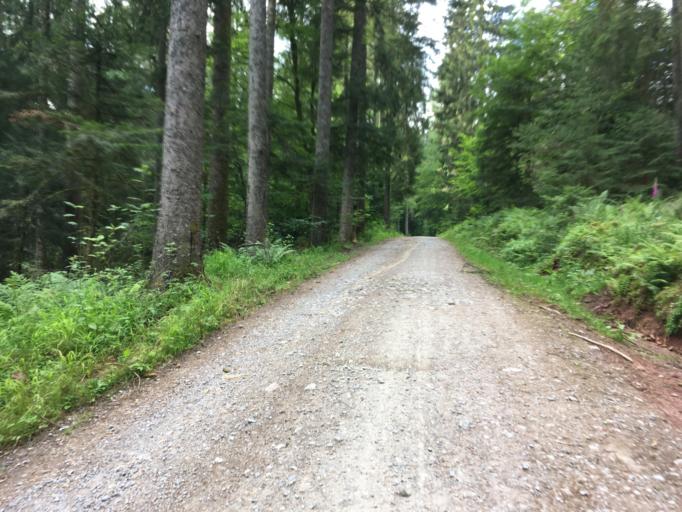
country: DE
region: Baden-Wuerttemberg
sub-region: Karlsruhe Region
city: Freudenstadt
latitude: 48.4392
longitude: 8.4058
